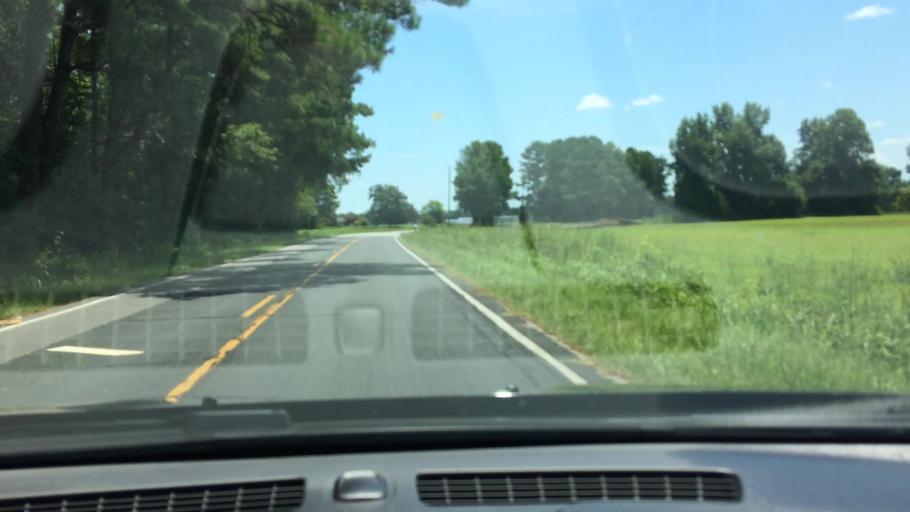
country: US
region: North Carolina
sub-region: Beaufort County
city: Washington
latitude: 35.5974
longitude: -77.1506
